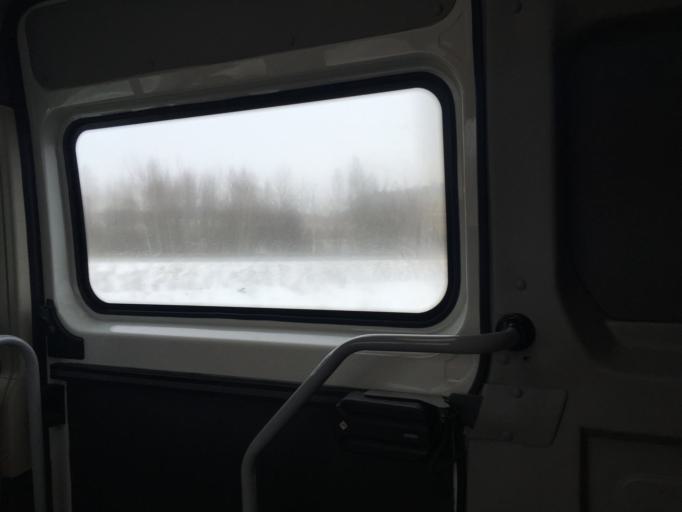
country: RU
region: Tula
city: Kosaya Gora
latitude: 54.1570
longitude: 37.4987
